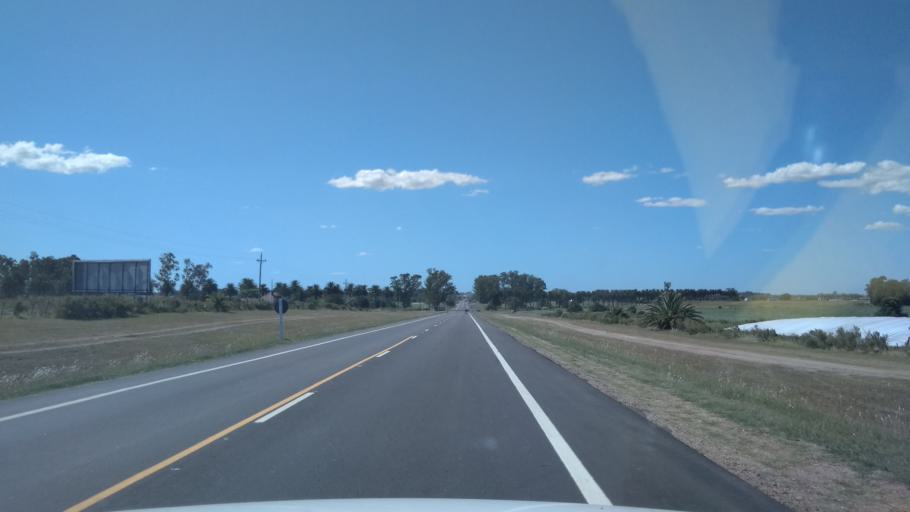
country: UY
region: Florida
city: Cardal
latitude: -34.3440
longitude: -56.2466
